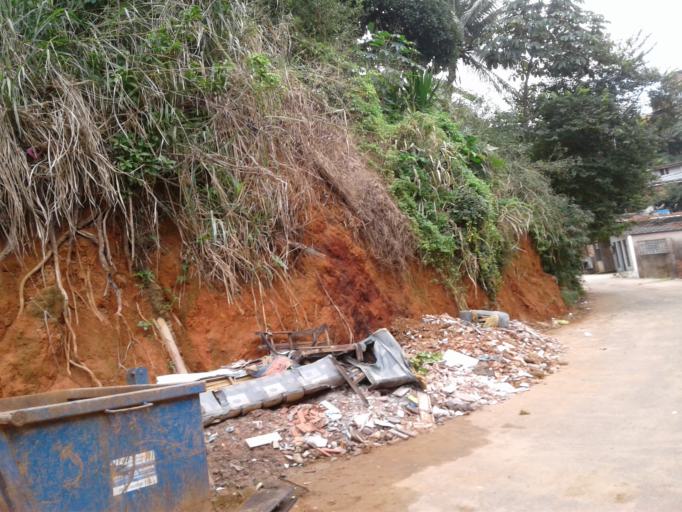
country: BR
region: Bahia
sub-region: Salvador
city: Salvador
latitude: -12.9116
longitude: -38.4741
